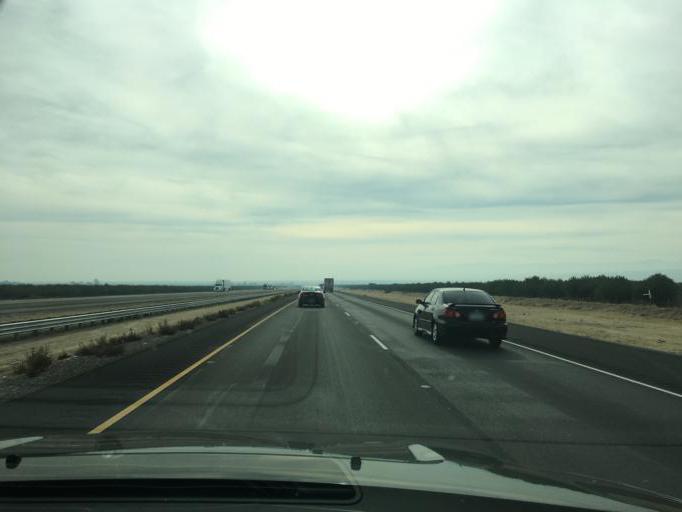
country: US
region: California
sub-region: Fresno County
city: Firebaugh
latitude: 36.6756
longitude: -120.6506
